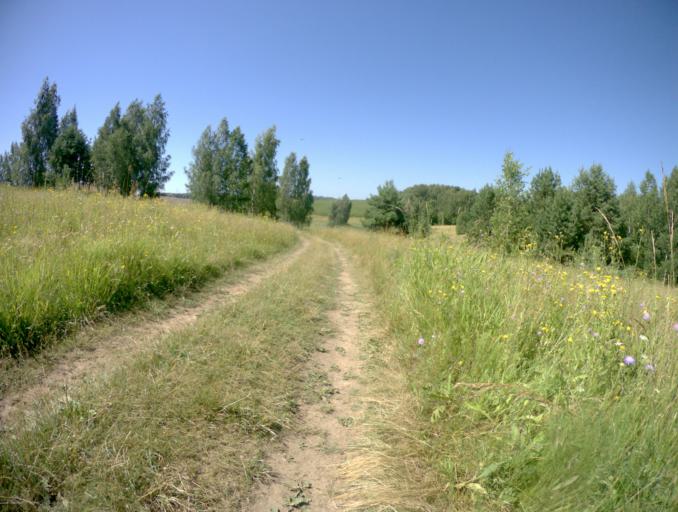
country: RU
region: Nizjnij Novgorod
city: Reshetikha
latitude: 56.1354
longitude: 43.2888
